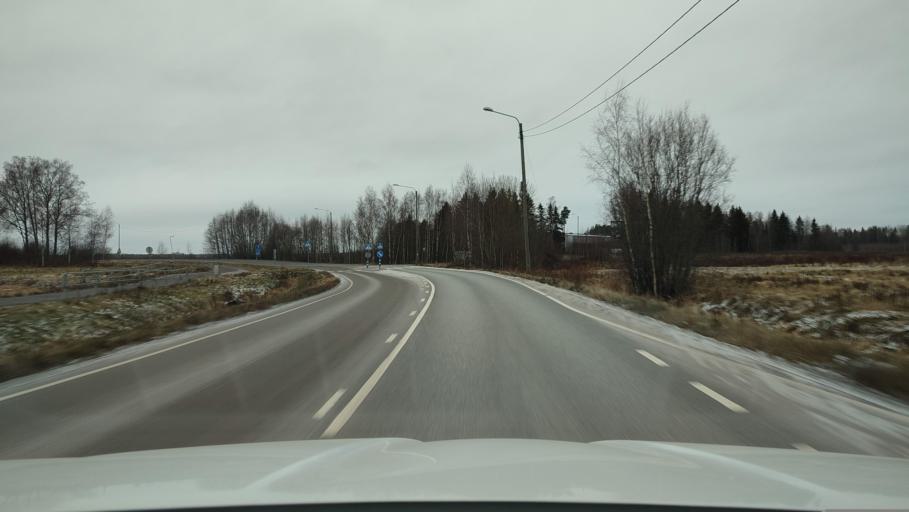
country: FI
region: Ostrobothnia
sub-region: Vaasa
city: Ristinummi
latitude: 63.0361
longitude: 21.7840
